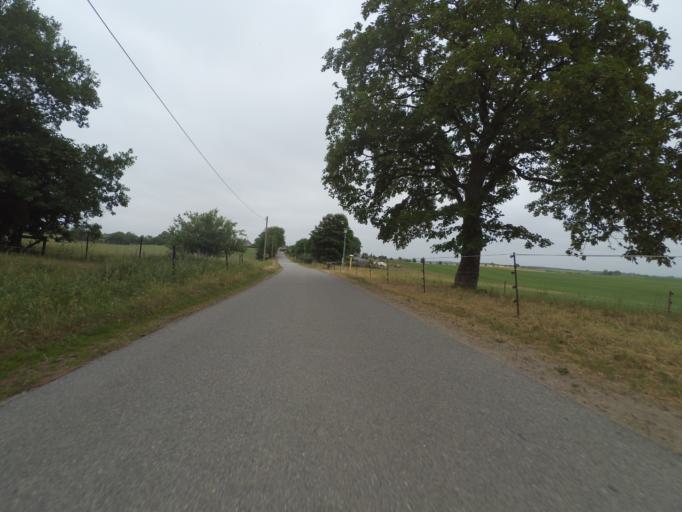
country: DE
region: Mecklenburg-Vorpommern
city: Goldberg
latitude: 53.5602
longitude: 12.1127
